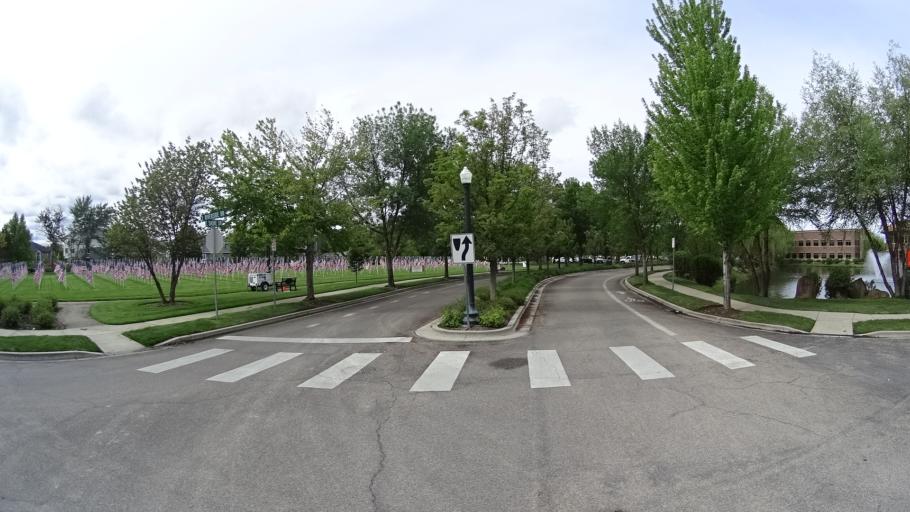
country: US
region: Idaho
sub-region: Ada County
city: Eagle
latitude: 43.6889
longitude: -116.3453
